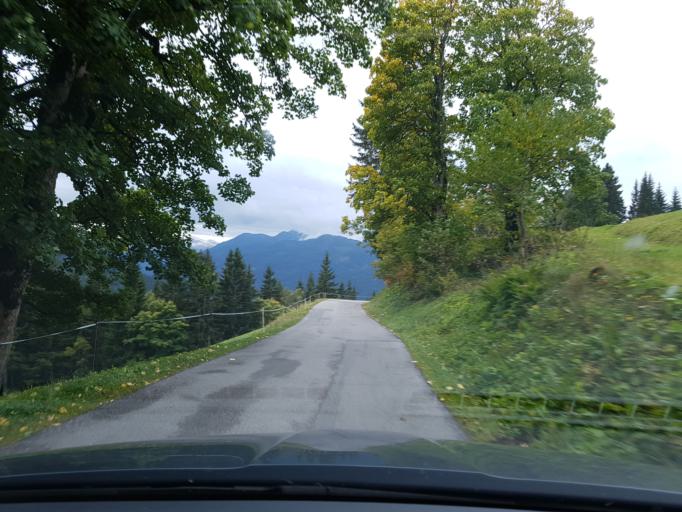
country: AT
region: Salzburg
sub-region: Politischer Bezirk Sankt Johann im Pongau
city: Filzmoos
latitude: 47.3993
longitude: 13.4970
